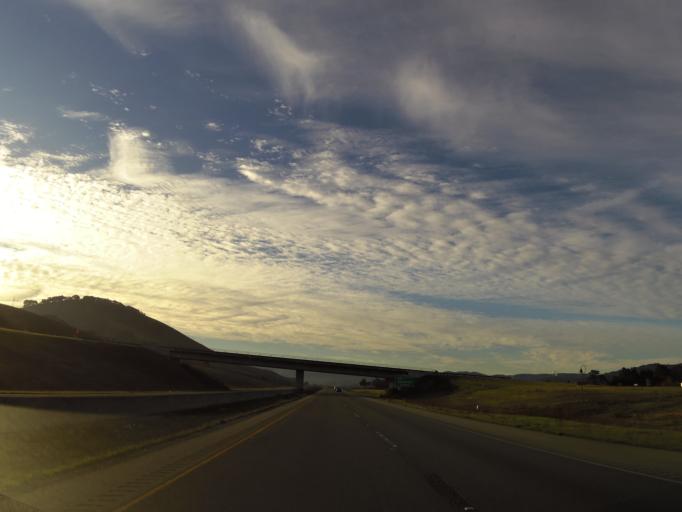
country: US
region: California
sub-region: San Benito County
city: San Juan Bautista
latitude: 36.9060
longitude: -121.5569
